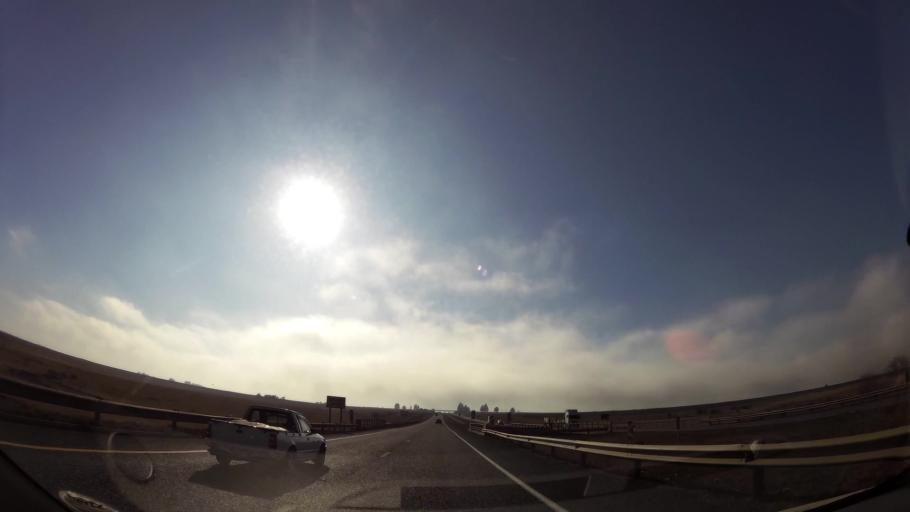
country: ZA
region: Mpumalanga
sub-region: Nkangala District Municipality
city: Delmas
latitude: -26.0282
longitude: 28.8737
